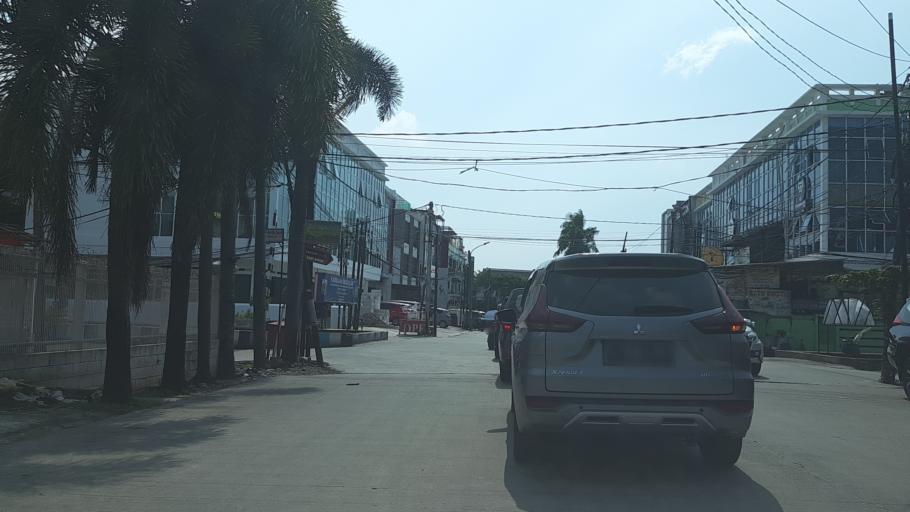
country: ID
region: Jakarta Raya
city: Jakarta
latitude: -6.1698
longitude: 106.7679
